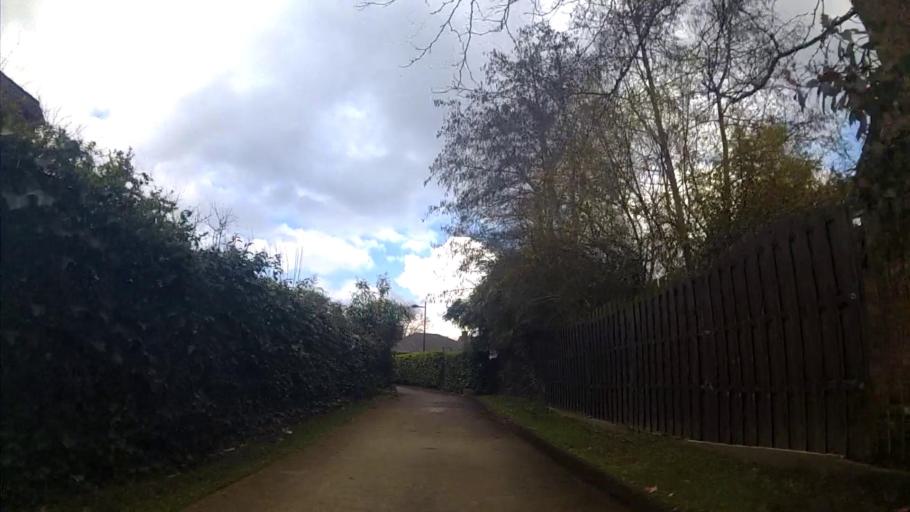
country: BE
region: Flanders
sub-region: Provincie Oost-Vlaanderen
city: Destelbergen
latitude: 51.0717
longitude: 3.7801
